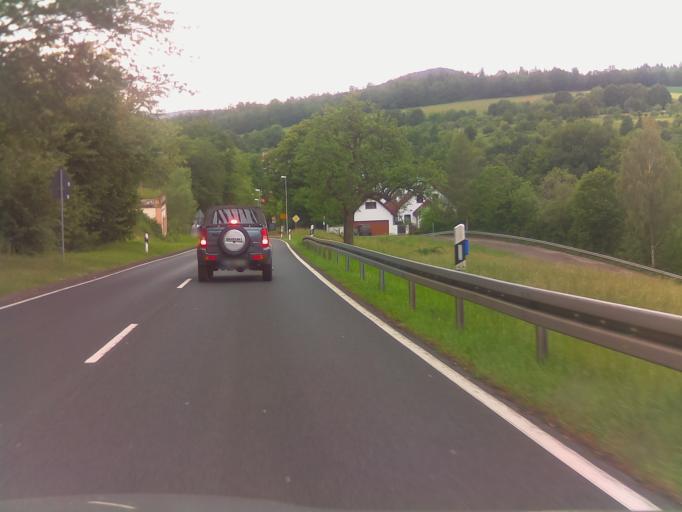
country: DE
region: Bavaria
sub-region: Regierungsbezirk Unterfranken
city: Laufach
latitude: 50.0291
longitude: 9.2784
